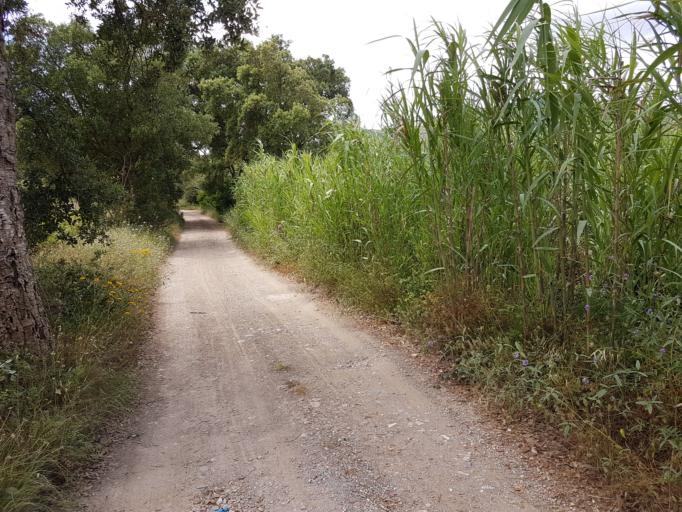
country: IT
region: Tuscany
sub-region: Provincia di Livorno
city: Portoferraio
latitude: 42.7885
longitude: 10.3490
